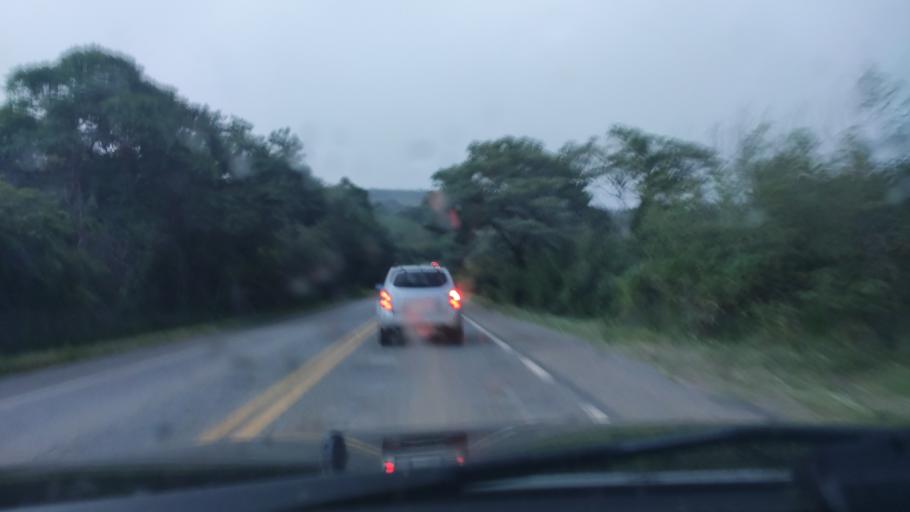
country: BR
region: Sao Paulo
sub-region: Braganca Paulista
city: Braganca Paulista
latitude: -22.8067
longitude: -46.5519
